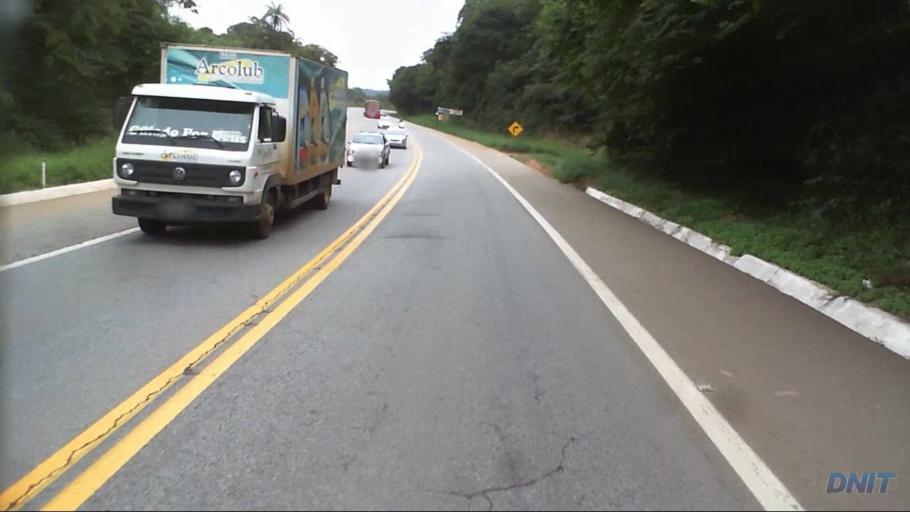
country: BR
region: Minas Gerais
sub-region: Barao De Cocais
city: Barao de Cocais
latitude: -19.7487
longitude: -43.4887
